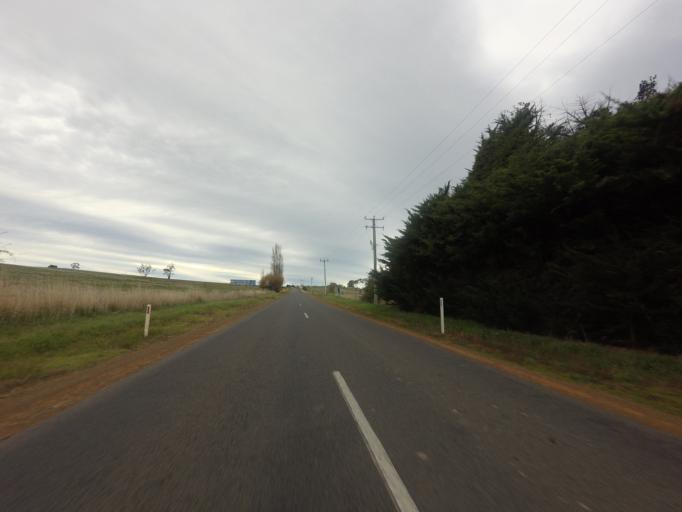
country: AU
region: Tasmania
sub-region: Derwent Valley
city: New Norfolk
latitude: -42.5335
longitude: 146.7526
